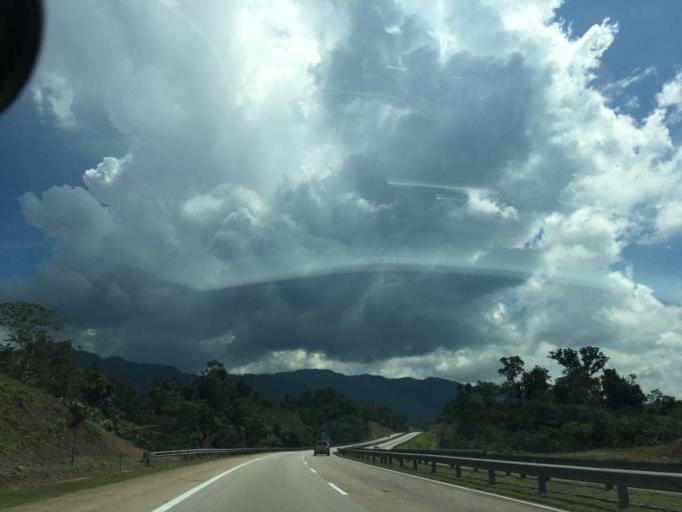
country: MY
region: Pahang
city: Kuantan
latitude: 3.7289
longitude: 102.9426
